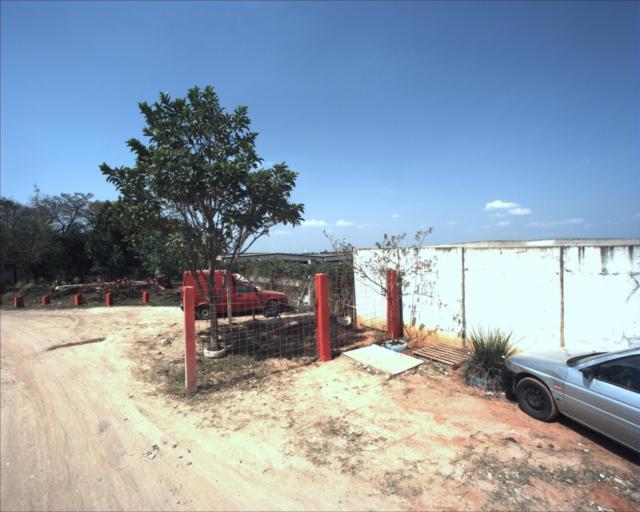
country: BR
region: Sao Paulo
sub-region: Sorocaba
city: Sorocaba
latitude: -23.4320
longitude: -47.4384
